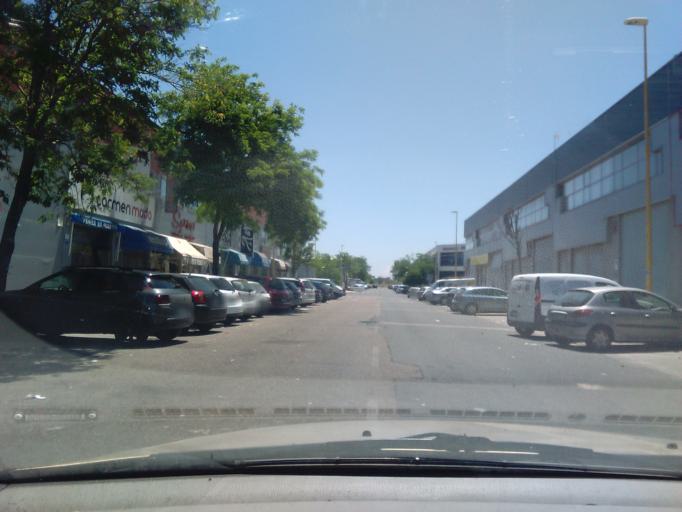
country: ES
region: Andalusia
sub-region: Provincia de Sevilla
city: Sevilla
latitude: 37.3828
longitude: -5.9315
